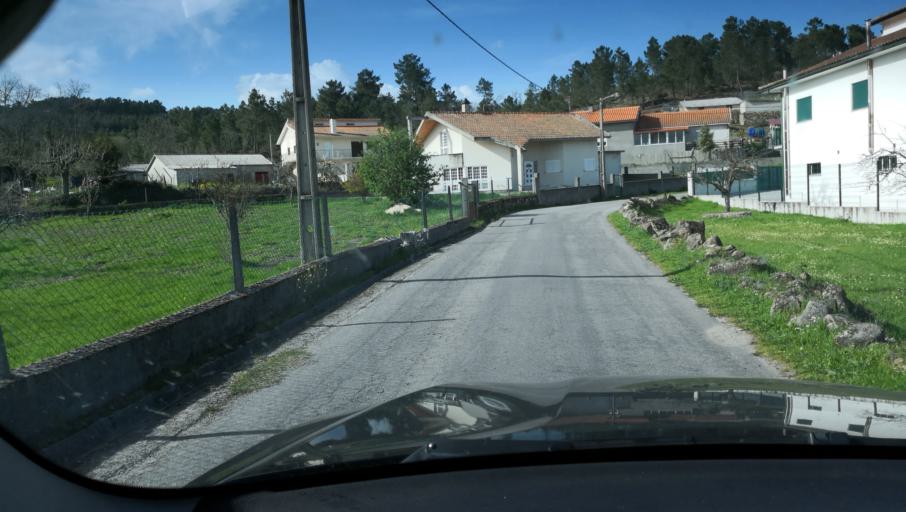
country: PT
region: Vila Real
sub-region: Vila Real
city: Vila Real
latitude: 41.2830
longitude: -7.6690
